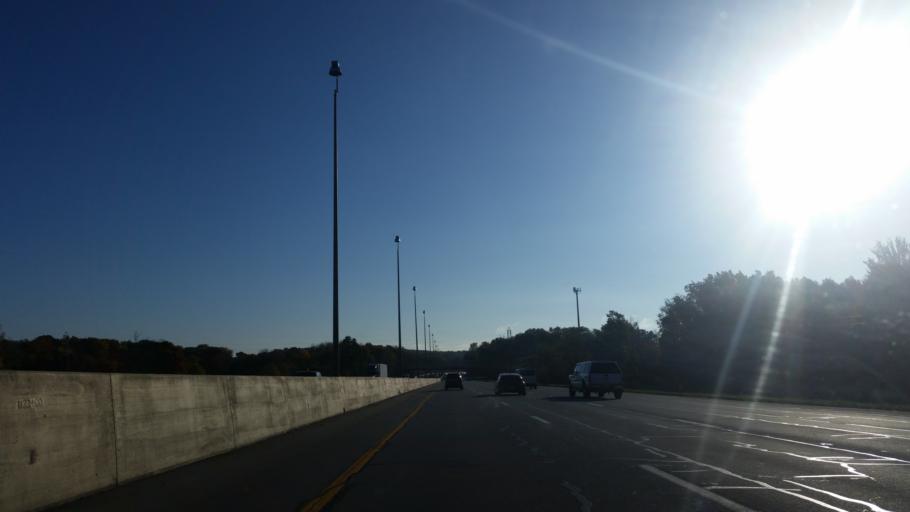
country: US
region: Ohio
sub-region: Summit County
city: Fairlawn
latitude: 41.1191
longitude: -81.6344
